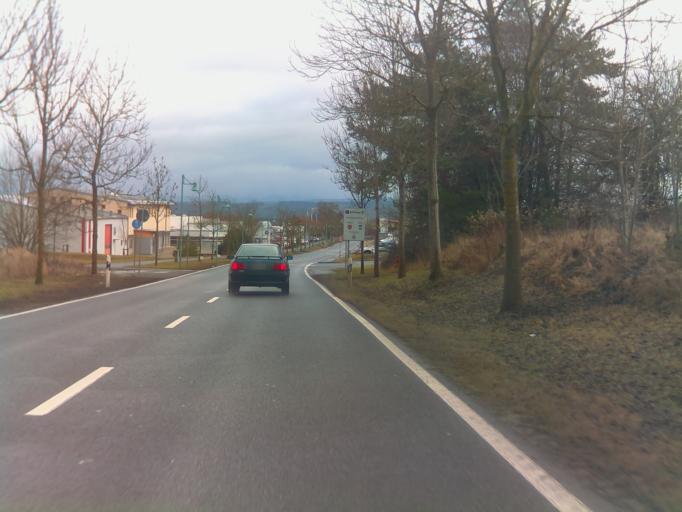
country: DE
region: Thuringia
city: Sulzfeld
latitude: 50.5614
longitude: 10.3647
